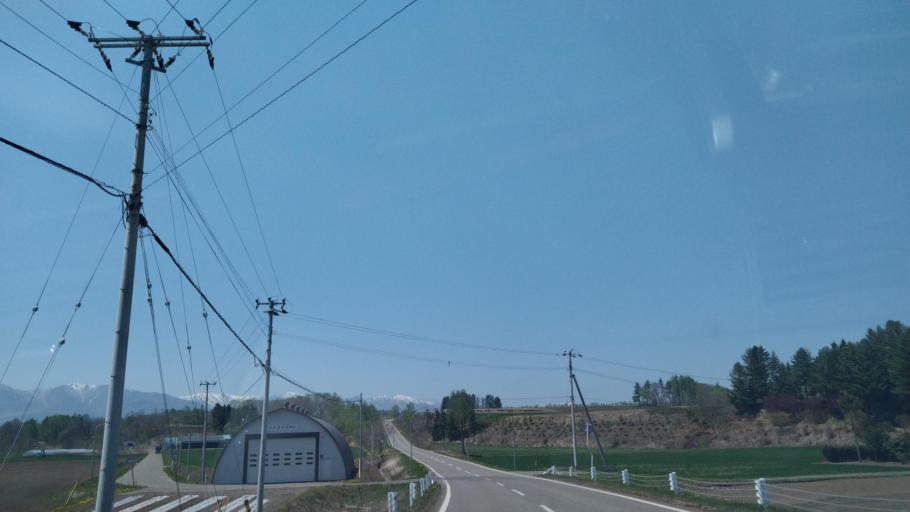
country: JP
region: Hokkaido
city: Obihiro
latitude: 42.9029
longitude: 143.0097
